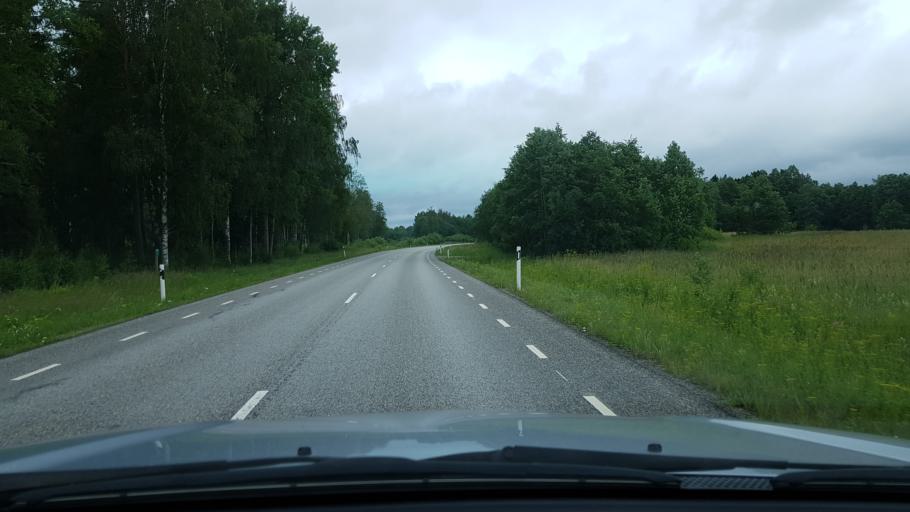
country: EE
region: Ida-Virumaa
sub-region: Narva-Joesuu linn
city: Narva-Joesuu
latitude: 59.3489
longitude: 27.9316
